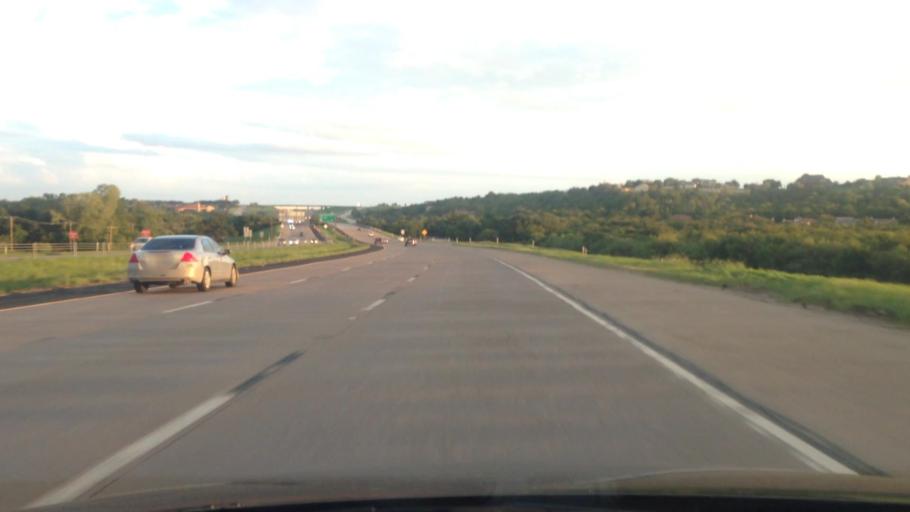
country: US
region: Texas
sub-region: Tarrant County
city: White Settlement
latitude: 32.7169
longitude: -97.4792
